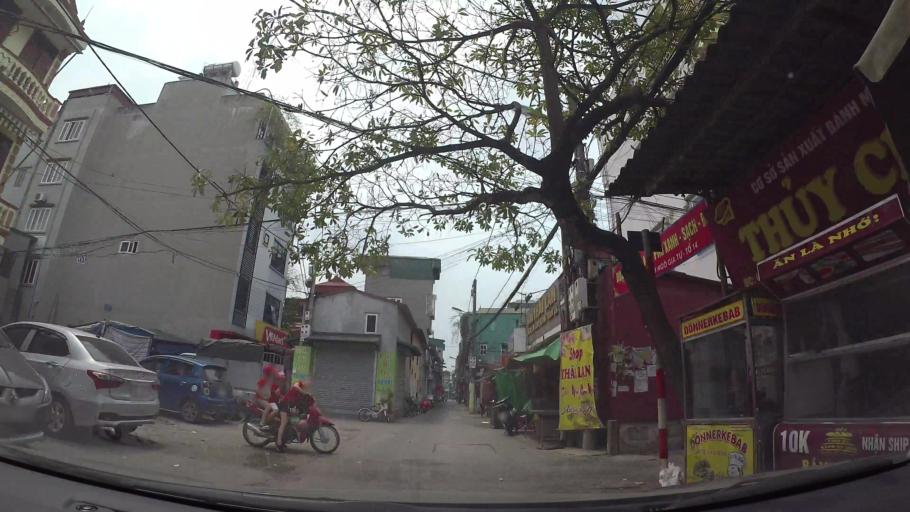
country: VN
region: Ha Noi
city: Trau Quy
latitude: 21.0705
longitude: 105.9056
